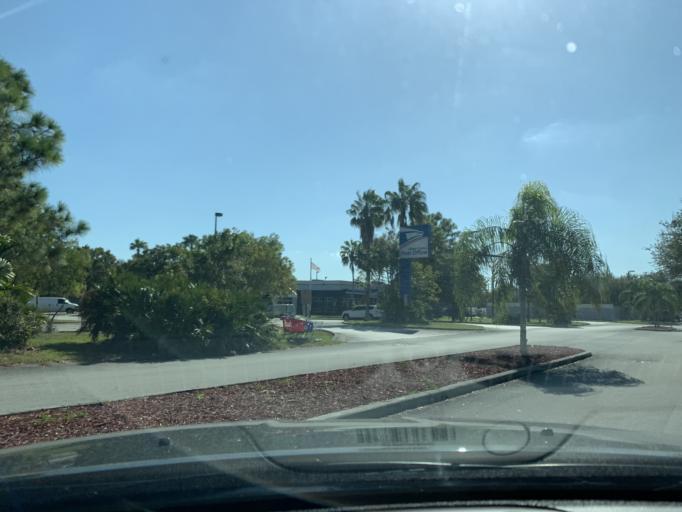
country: US
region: Florida
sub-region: Miami-Dade County
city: Country Walk
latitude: 25.6256
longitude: -80.4128
